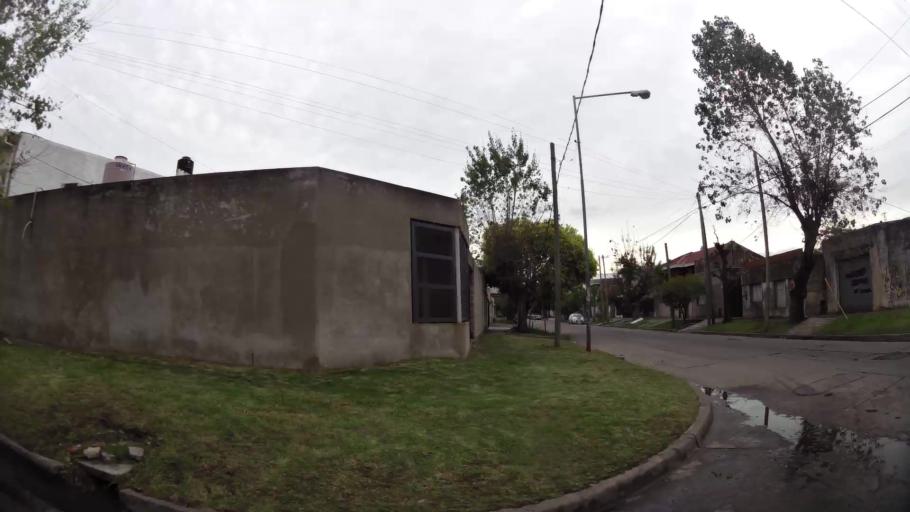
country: AR
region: Buenos Aires
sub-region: Partido de Lanus
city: Lanus
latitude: -34.7006
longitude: -58.3694
